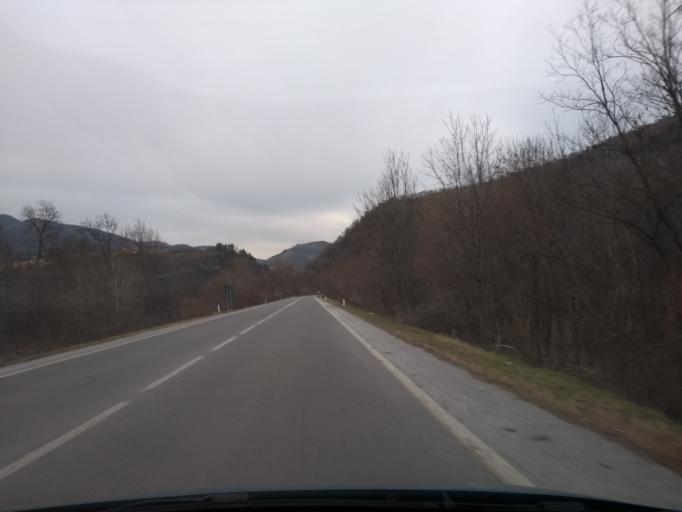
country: IT
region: Piedmont
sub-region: Provincia di Torino
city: Germagnano
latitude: 45.2622
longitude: 7.4748
